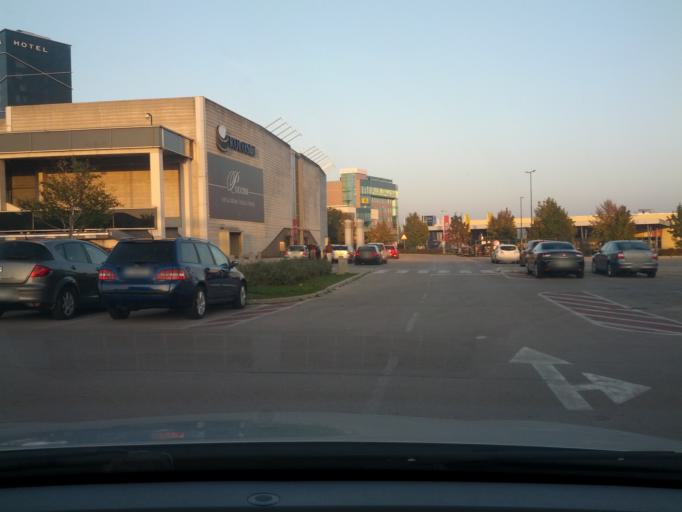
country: SI
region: Ljubljana
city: Ljubljana
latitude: 46.0648
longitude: 14.5494
